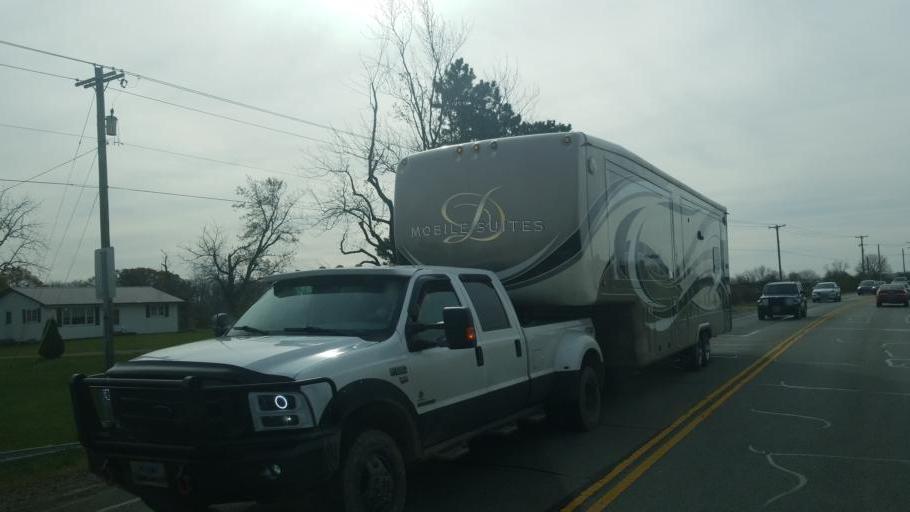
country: US
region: Ohio
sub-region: Madison County
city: London
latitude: 39.9103
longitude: -83.4243
